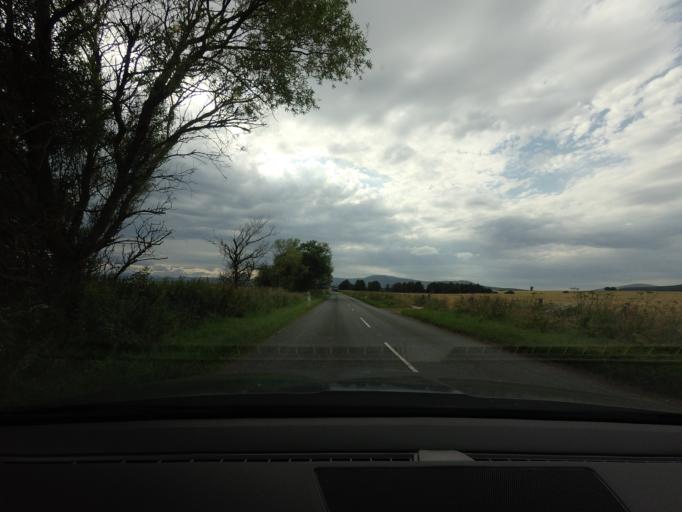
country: GB
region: Scotland
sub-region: Highland
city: Alness
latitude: 57.6914
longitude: -4.2163
